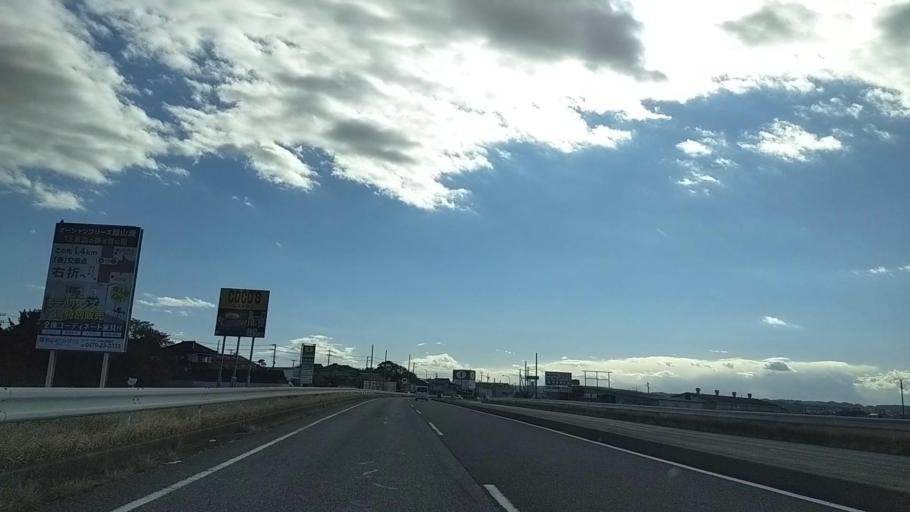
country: JP
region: Chiba
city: Tateyama
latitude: 35.0208
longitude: 139.8696
